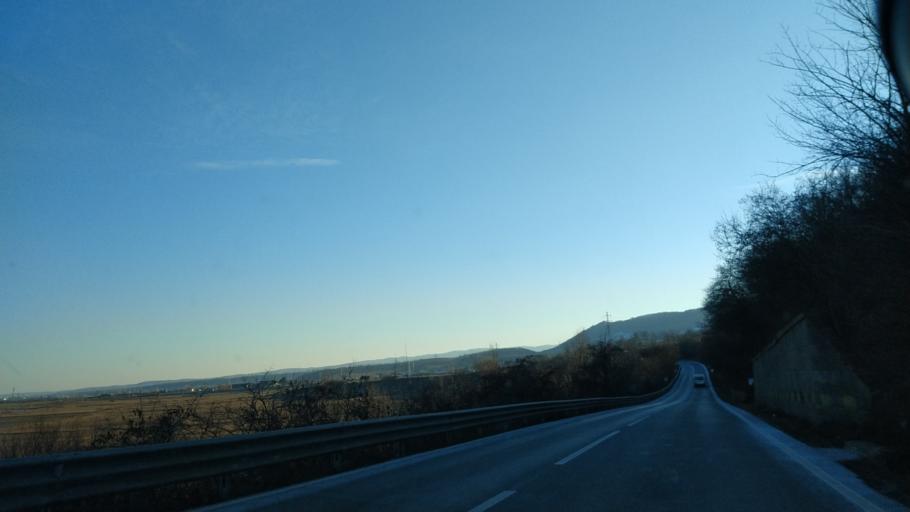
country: RO
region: Bacau
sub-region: Comuna Helegiu
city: Bratila
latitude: 46.2942
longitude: 26.7516
